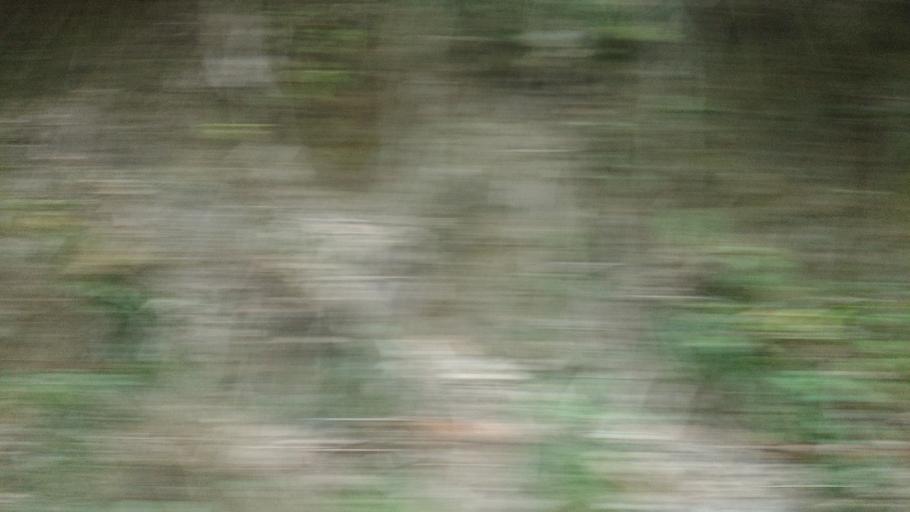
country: TW
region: Taiwan
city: Lugu
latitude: 23.6232
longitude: 120.7191
